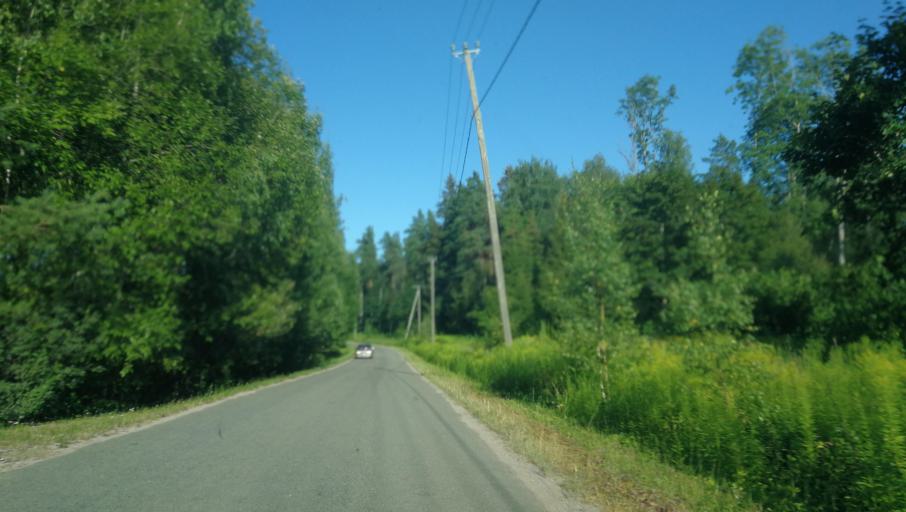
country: LV
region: Cesu Rajons
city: Cesis
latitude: 57.2880
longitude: 25.2229
